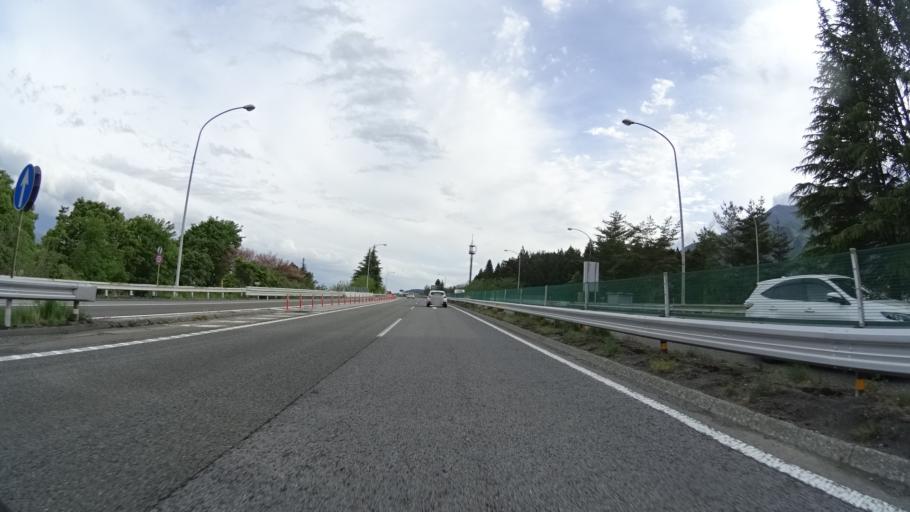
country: JP
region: Nagano
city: Ina
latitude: 35.7400
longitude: 137.9107
